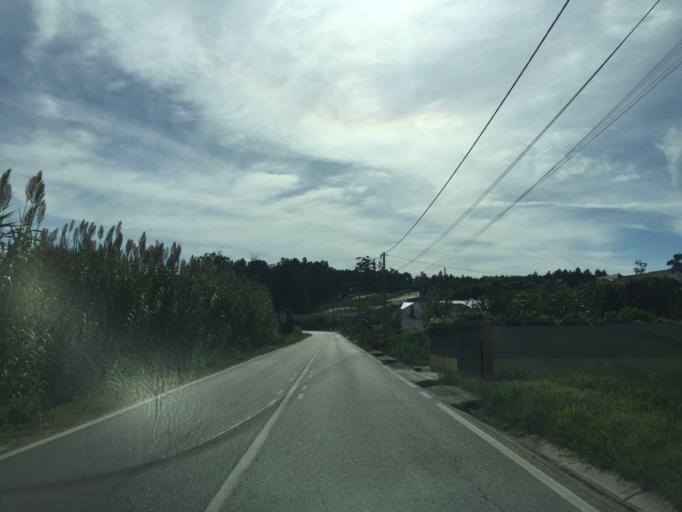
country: PT
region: Coimbra
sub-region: Figueira da Foz
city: Lavos
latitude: 40.1107
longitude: -8.8425
